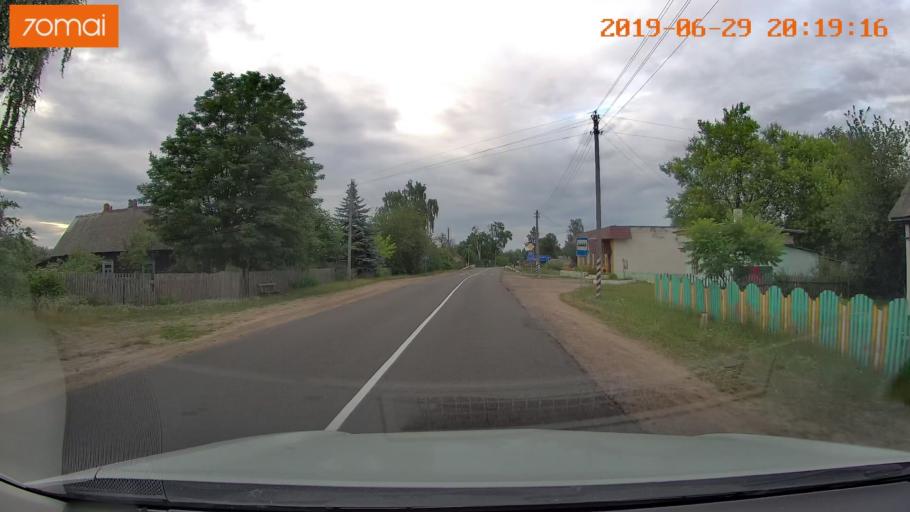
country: BY
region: Brest
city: Asnyezhytsy
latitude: 52.3996
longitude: 26.2436
